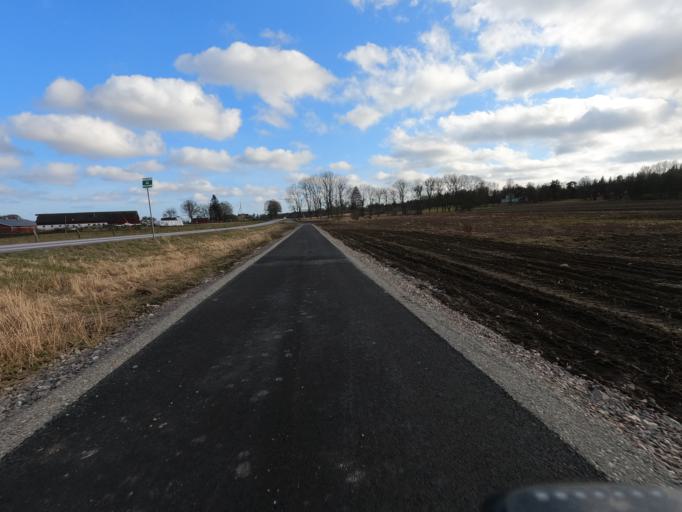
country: SE
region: Kronoberg
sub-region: Alvesta Kommun
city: Vislanda
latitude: 56.7251
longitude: 14.5774
